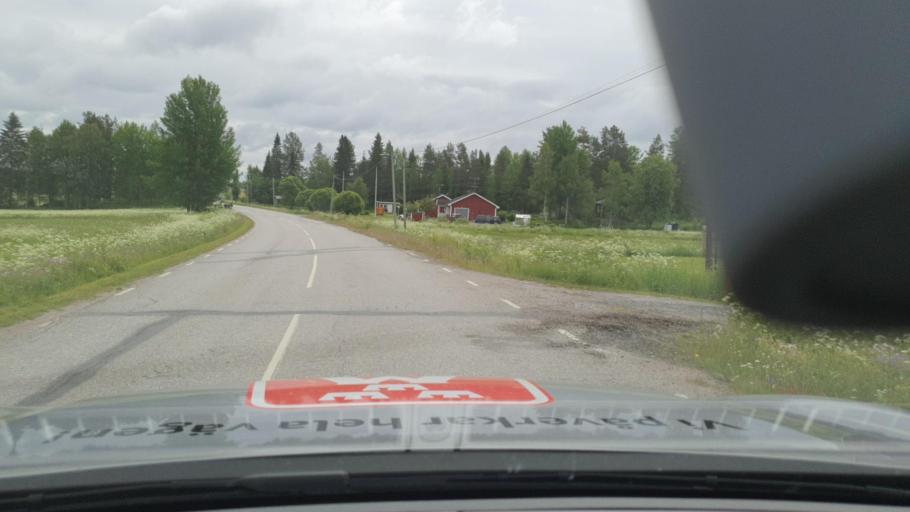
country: SE
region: Norrbotten
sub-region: Lulea Kommun
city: Ranea
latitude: 65.9180
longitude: 22.1528
